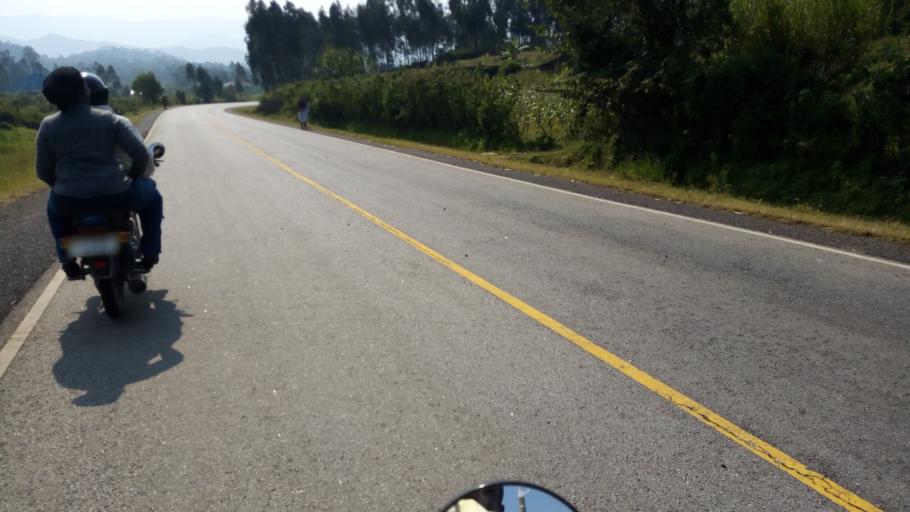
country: UG
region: Western Region
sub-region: Kisoro District
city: Kisoro
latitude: -1.3293
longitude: 29.7306
